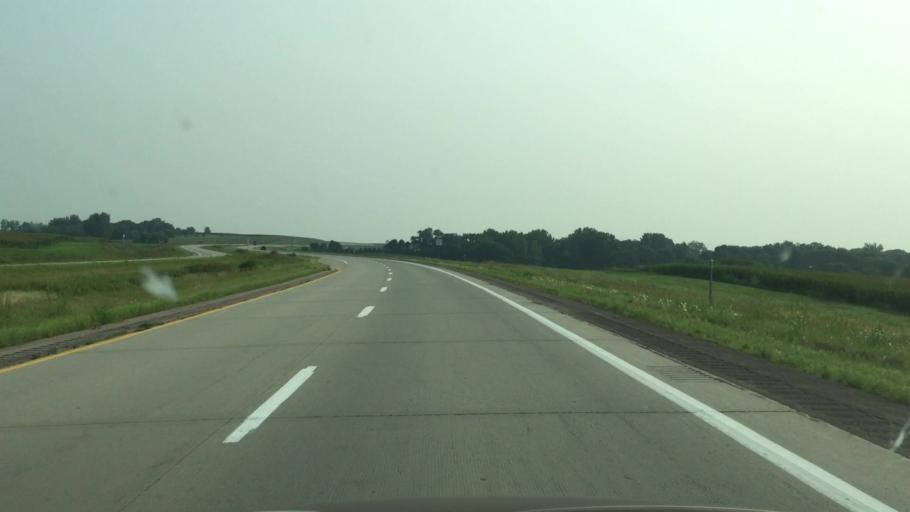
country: US
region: Iowa
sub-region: Plymouth County
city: Le Mars
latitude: 42.8492
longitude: -96.1386
